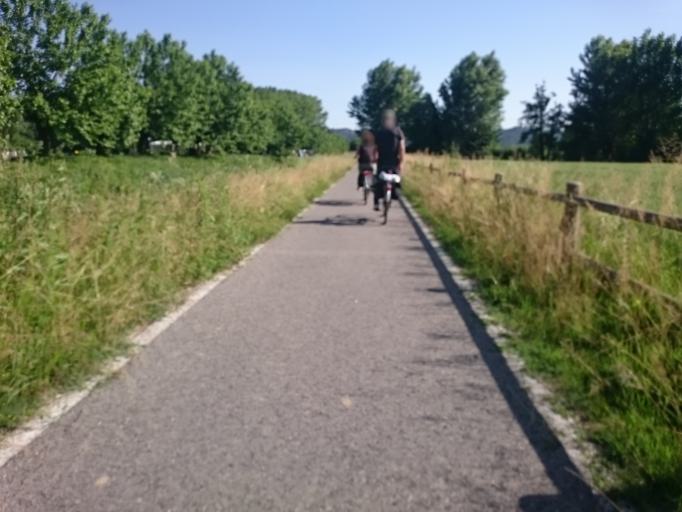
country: IT
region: Veneto
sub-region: Provincia di Padova
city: Torreglia
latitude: 45.3441
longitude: 11.7454
